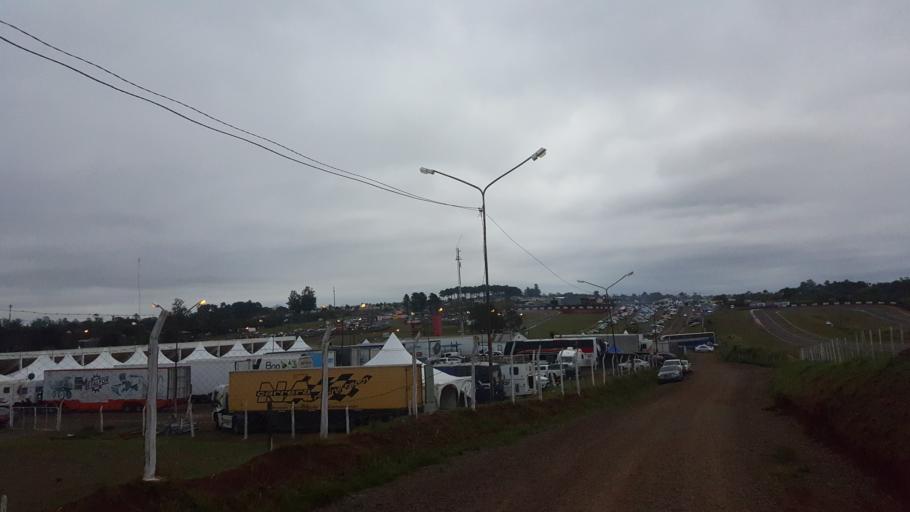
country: AR
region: Misiones
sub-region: Departamento de Capital
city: Posadas
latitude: -27.4401
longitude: -55.9256
